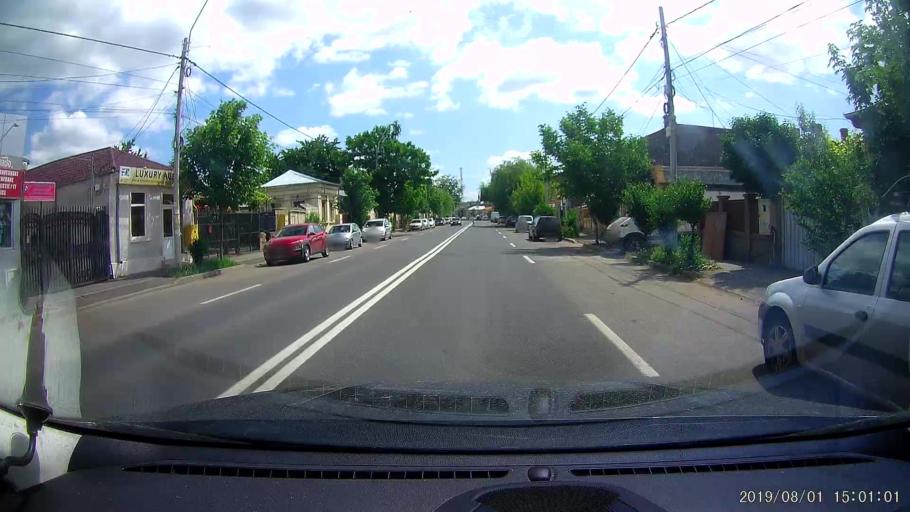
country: RO
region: Braila
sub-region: Municipiul Braila
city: Braila
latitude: 45.2753
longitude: 27.9614
